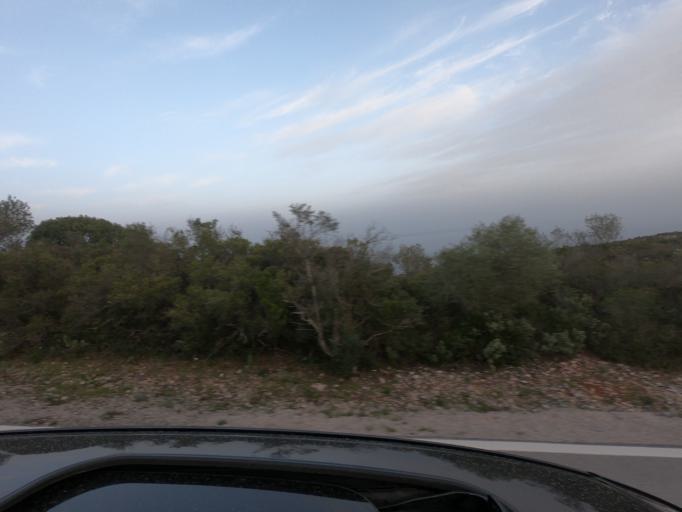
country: PT
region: Setubal
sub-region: Palmela
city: Quinta do Anjo
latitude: 38.4868
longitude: -8.9874
